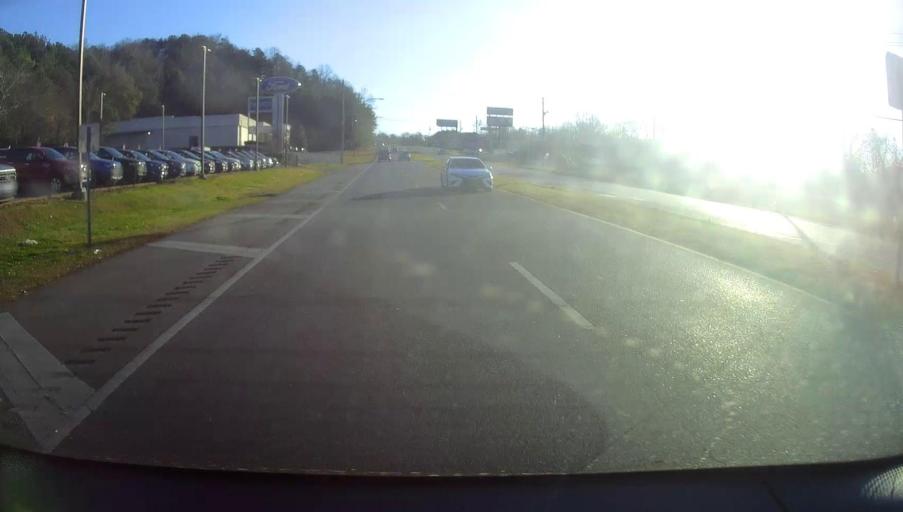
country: US
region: Alabama
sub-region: Calhoun County
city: Oxford
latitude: 33.6275
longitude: -85.8269
